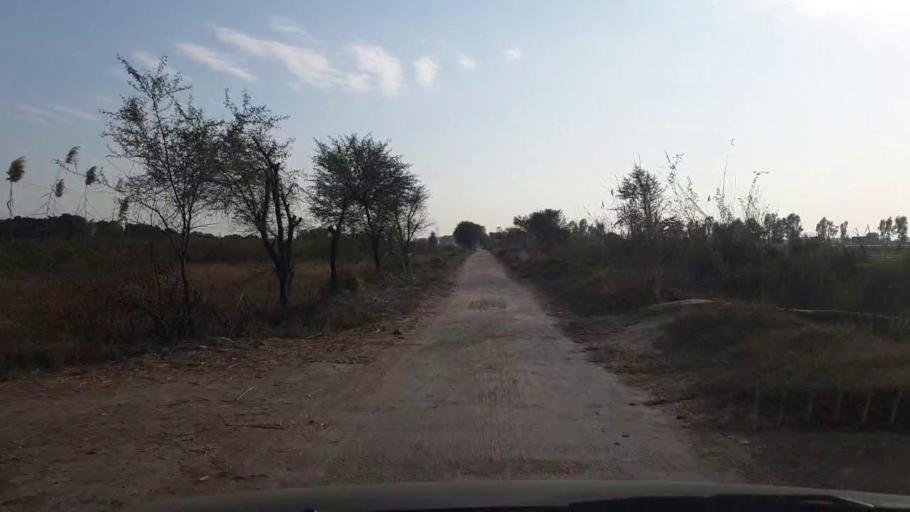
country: PK
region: Sindh
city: Sakrand
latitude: 26.0171
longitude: 68.3536
